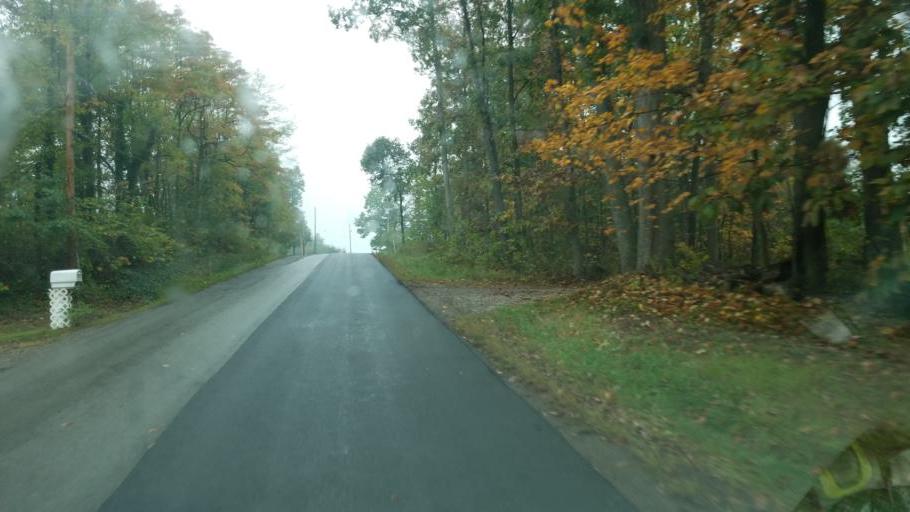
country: US
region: Ohio
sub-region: Tuscarawas County
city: Sugarcreek
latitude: 40.5744
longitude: -81.7219
